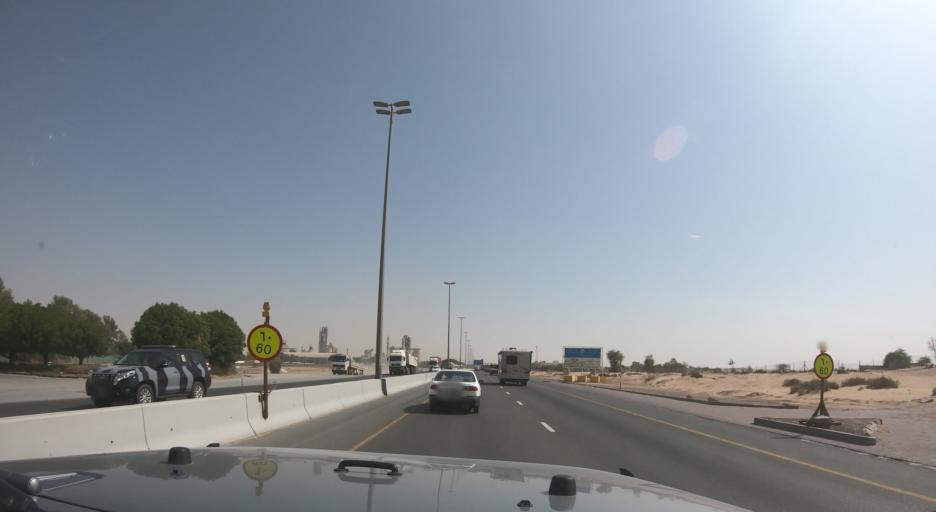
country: AE
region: Ash Shariqah
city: Sharjah
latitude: 25.2980
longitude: 55.6049
